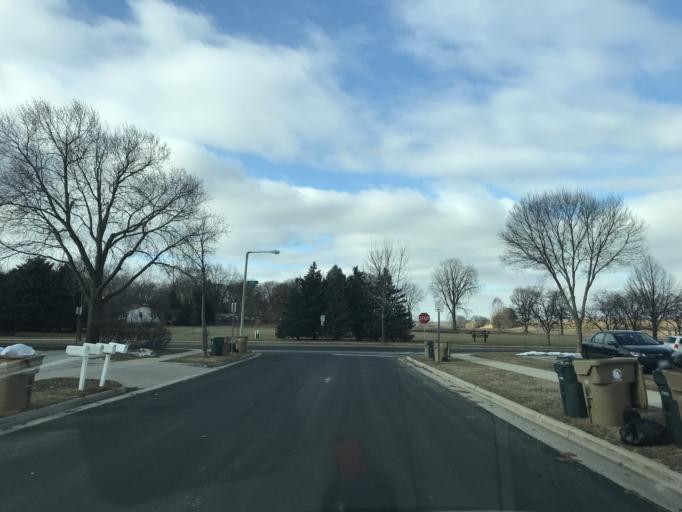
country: US
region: Wisconsin
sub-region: Dane County
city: Monona
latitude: 43.1101
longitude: -89.2987
